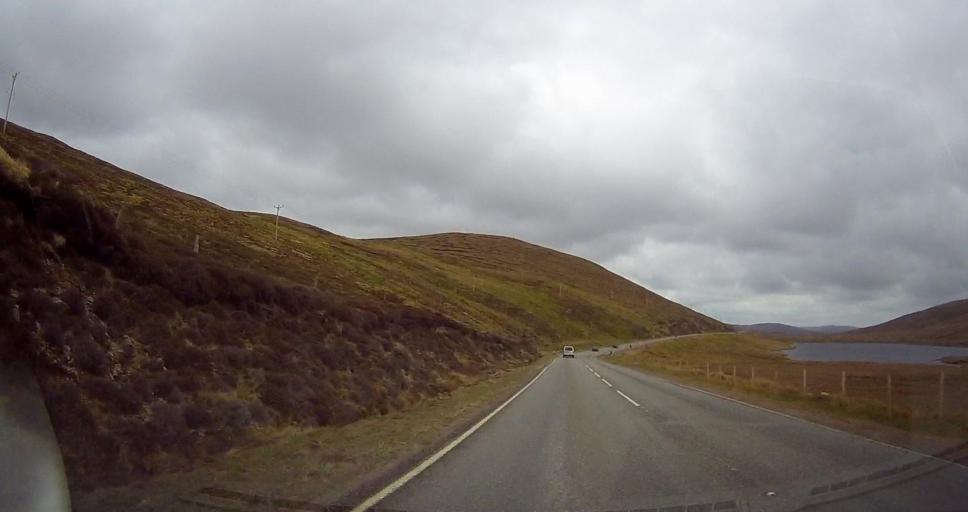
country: GB
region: Scotland
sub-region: Shetland Islands
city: Lerwick
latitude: 60.3198
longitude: -1.2486
